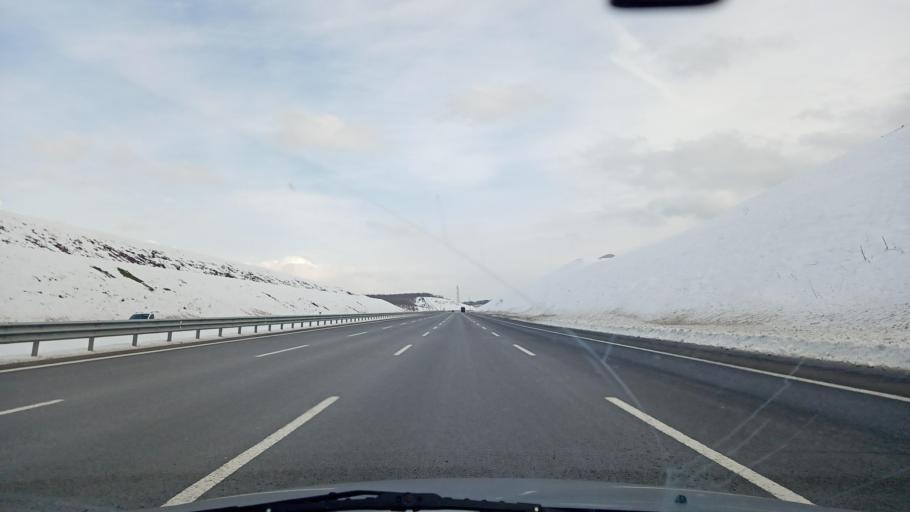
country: TR
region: Kocaeli
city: Hereke
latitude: 40.8959
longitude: 29.6268
